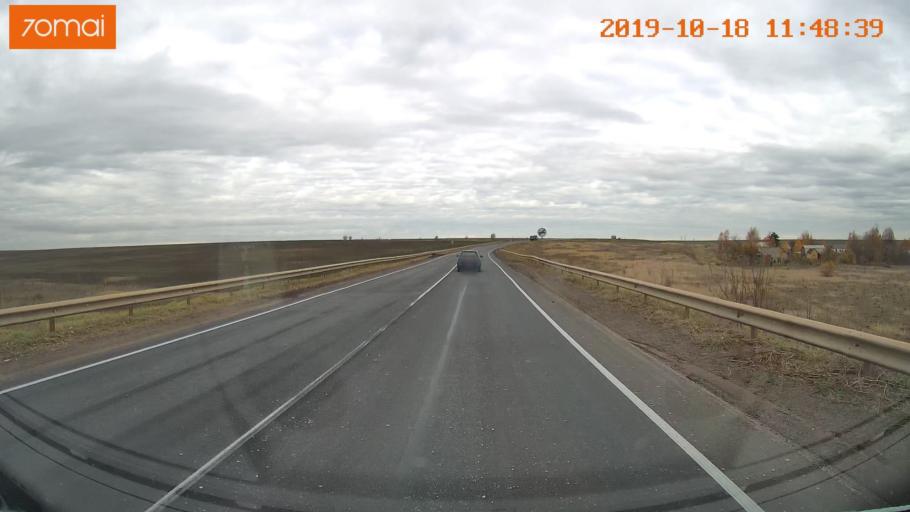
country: RU
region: Rjazan
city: Mikhaylov
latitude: 54.2408
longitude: 38.9844
